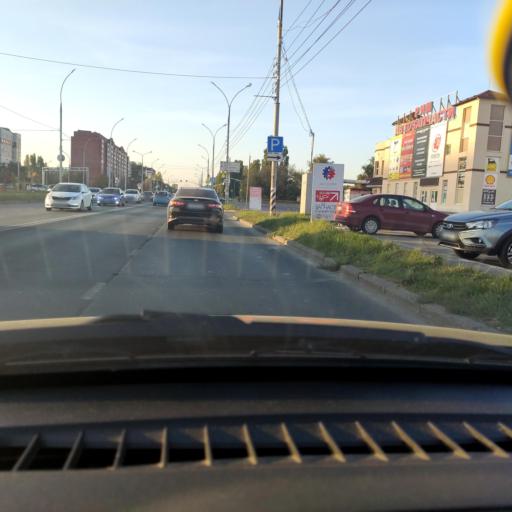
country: RU
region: Samara
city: Tol'yatti
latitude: 53.5443
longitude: 49.3162
